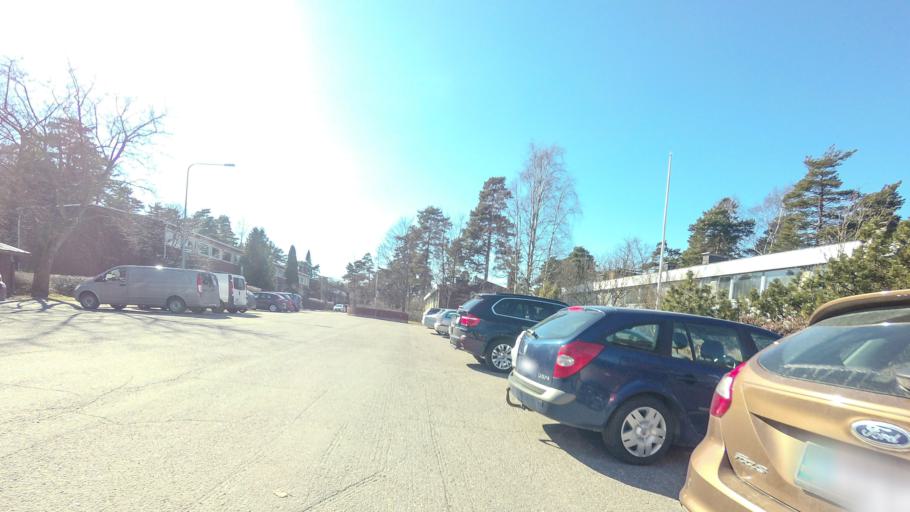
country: FI
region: Uusimaa
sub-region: Helsinki
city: Helsinki
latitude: 60.1903
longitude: 25.0113
